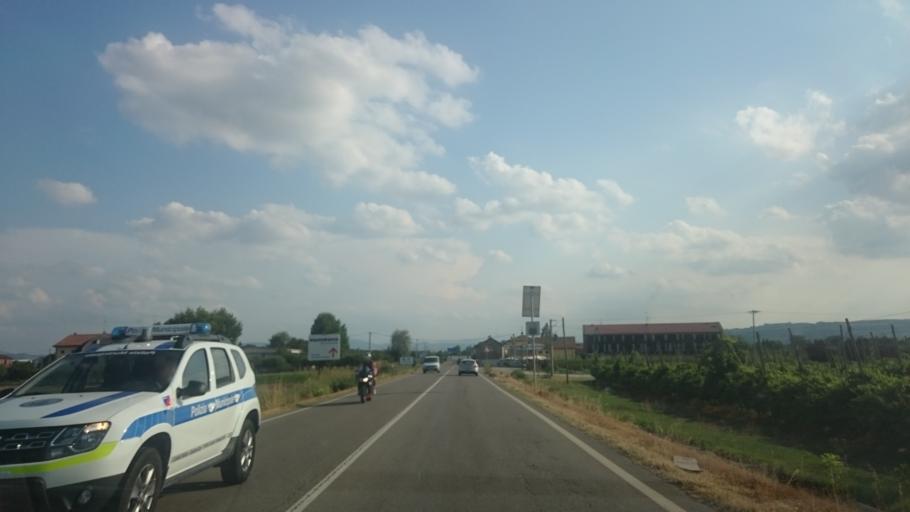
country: IT
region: Emilia-Romagna
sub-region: Provincia di Reggio Emilia
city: Salvaterra
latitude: 44.6094
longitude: 10.7777
